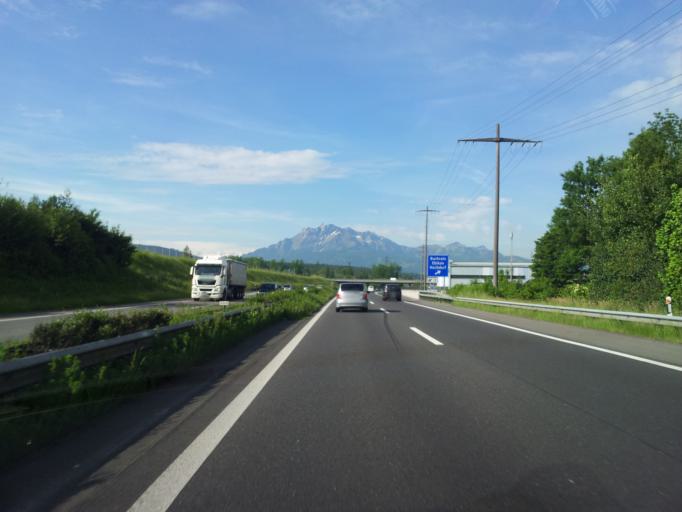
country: CH
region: Lucerne
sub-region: Lucerne-Land District
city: Buchrain
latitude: 47.1075
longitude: 8.3495
